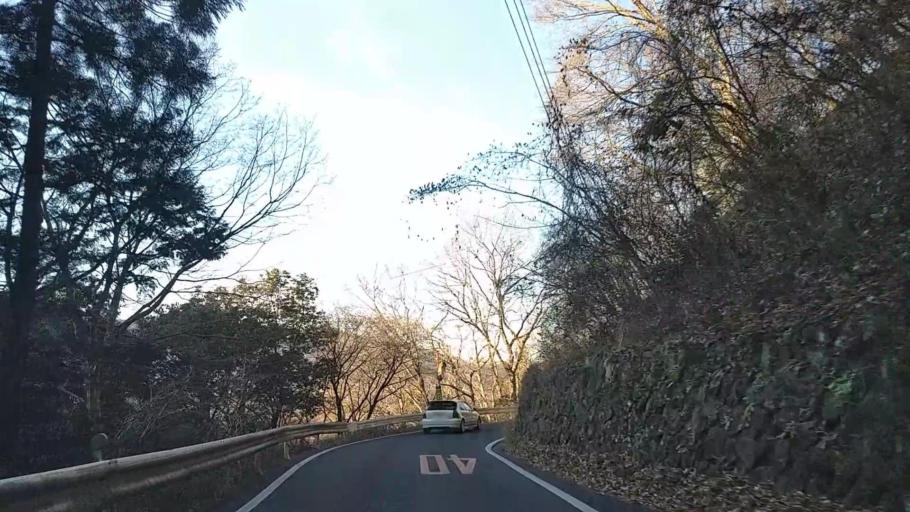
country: JP
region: Yamanashi
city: Uenohara
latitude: 35.5425
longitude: 139.1378
